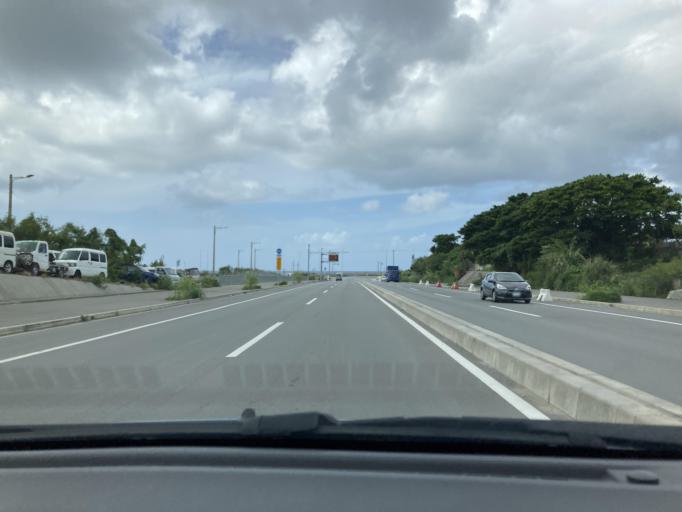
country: JP
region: Okinawa
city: Ginowan
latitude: 26.2701
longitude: 127.7085
